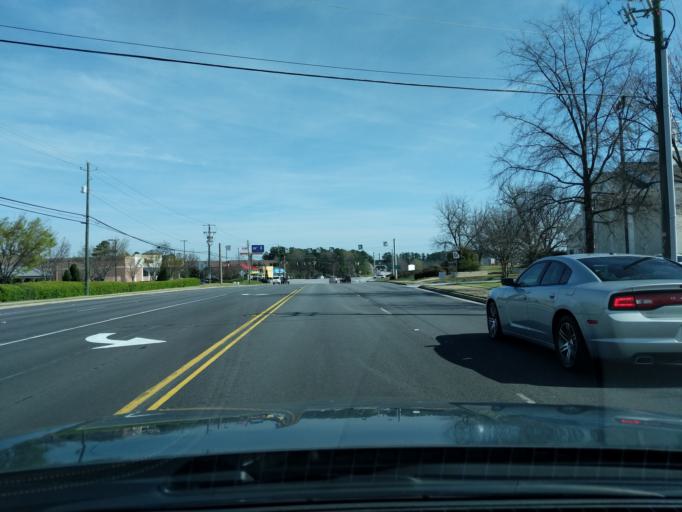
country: US
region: Georgia
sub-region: Columbia County
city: Evans
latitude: 33.5355
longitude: -82.1293
